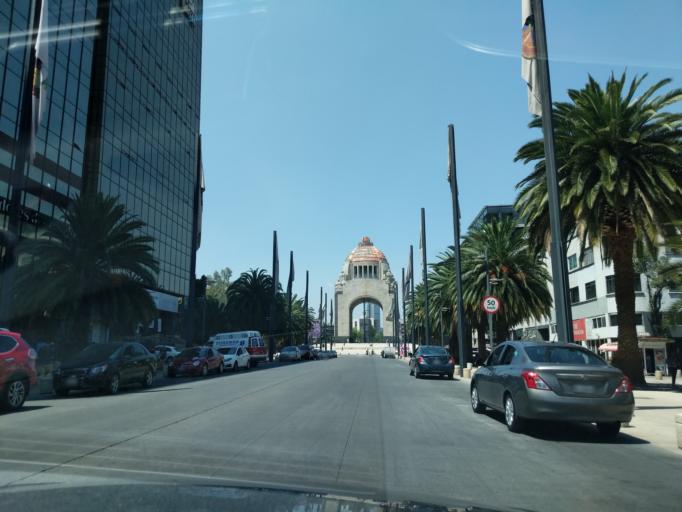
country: MX
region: Mexico City
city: Cuauhtemoc
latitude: 19.4358
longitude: -99.1517
